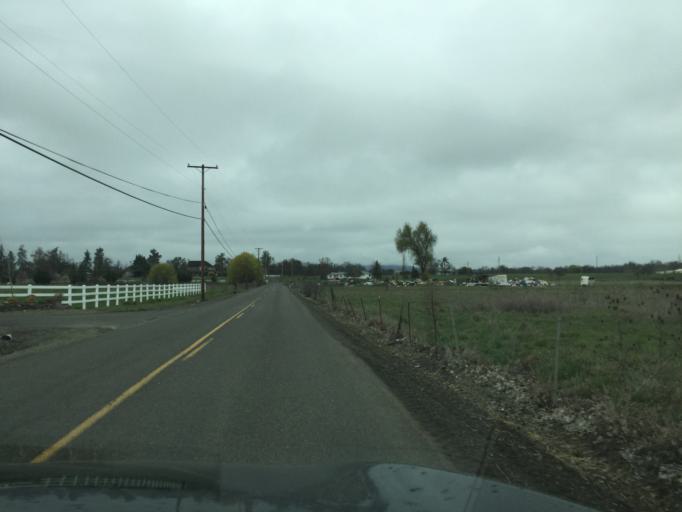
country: US
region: Oregon
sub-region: Jackson County
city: Central Point
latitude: 42.4048
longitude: -122.9089
